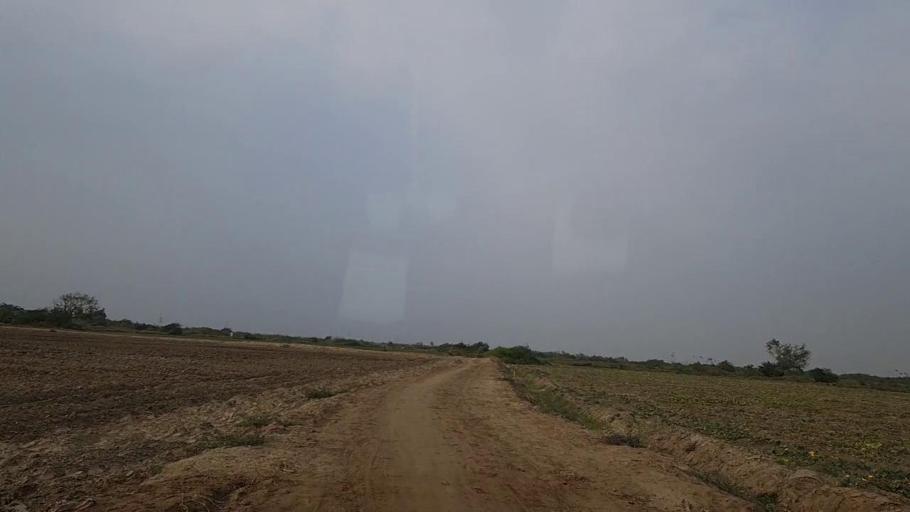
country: PK
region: Sindh
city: Mirpur Sakro
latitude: 24.6177
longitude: 67.5040
